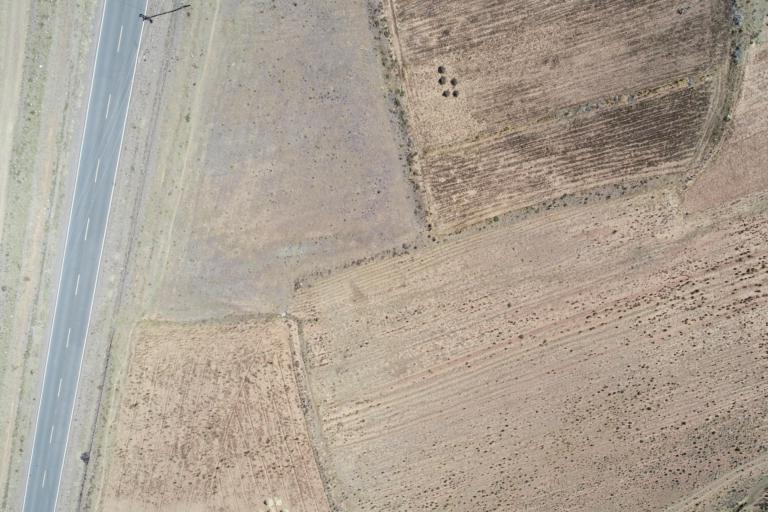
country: BO
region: La Paz
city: Achacachi
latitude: -15.9011
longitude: -68.8993
